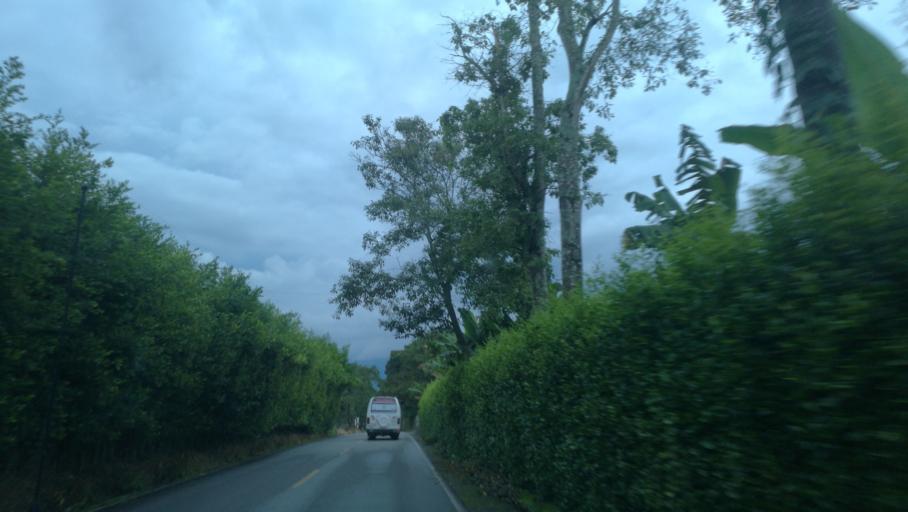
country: CO
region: Quindio
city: Montenegro
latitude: 4.5104
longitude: -75.7589
